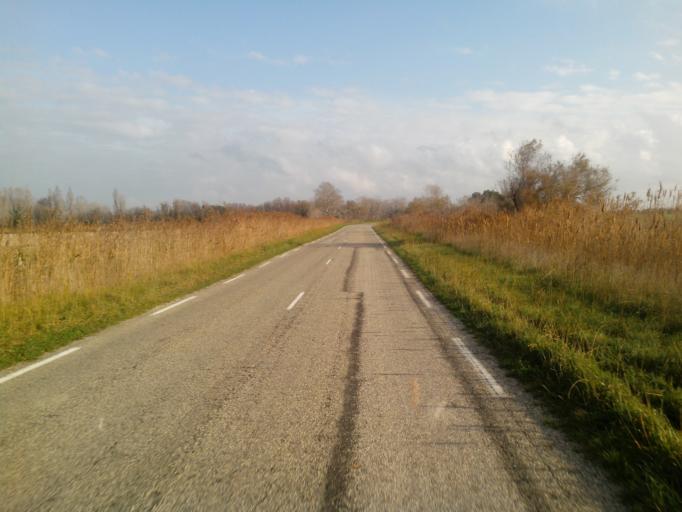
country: FR
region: Provence-Alpes-Cote d'Azur
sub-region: Departement des Bouches-du-Rhone
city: Arles
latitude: 43.5715
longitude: 4.5557
